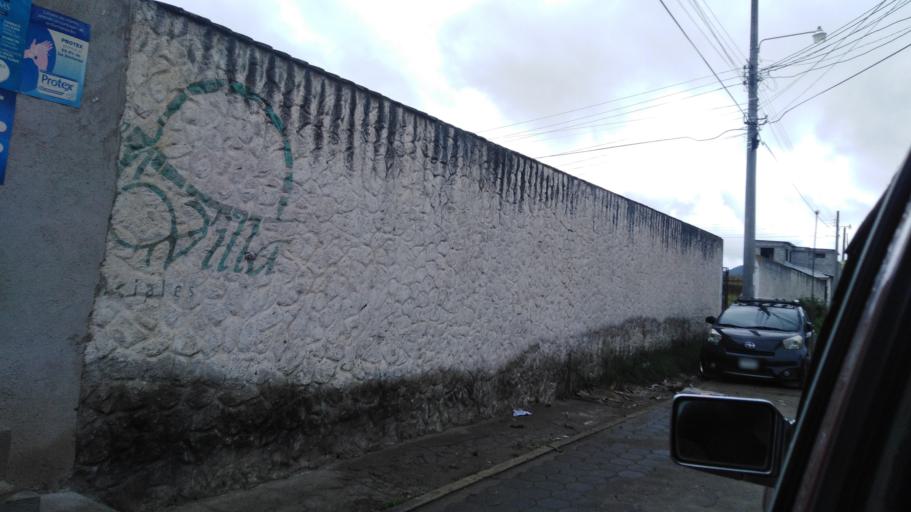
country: GT
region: Quetzaltenango
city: Quetzaltenango
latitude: 14.8529
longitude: -91.5060
